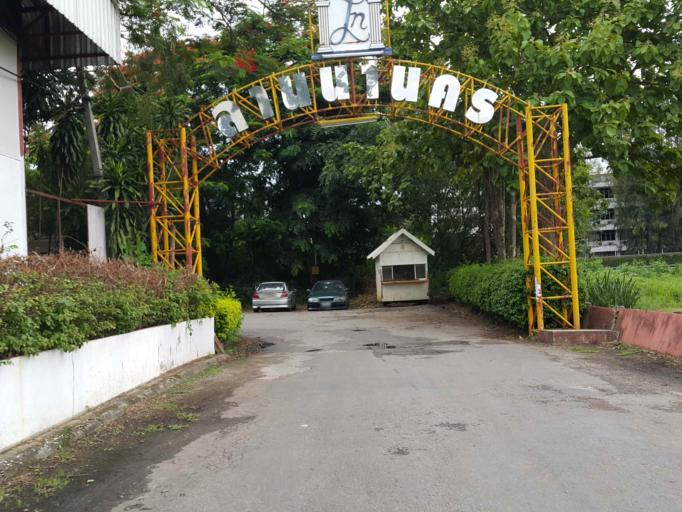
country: TH
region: Chiang Mai
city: Chiang Mai
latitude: 18.8158
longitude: 98.9952
